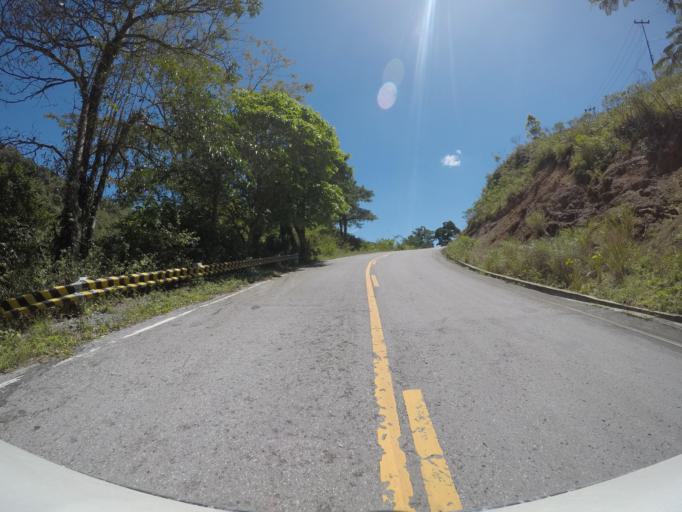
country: TL
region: Manatuto
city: Manatuto
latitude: -8.7646
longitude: 125.9673
